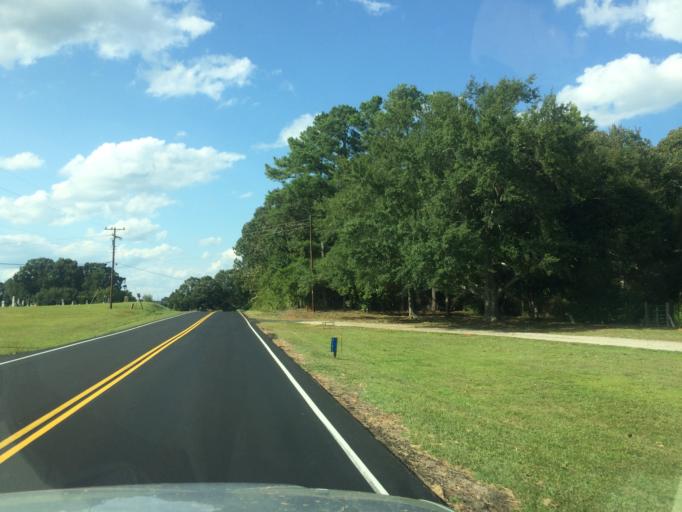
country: US
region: South Carolina
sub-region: Greenwood County
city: Ware Shoals
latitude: 34.4913
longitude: -82.1791
